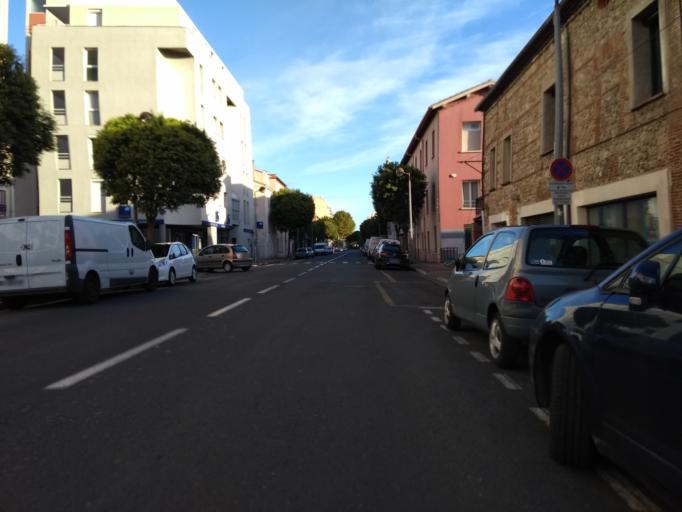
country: FR
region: Languedoc-Roussillon
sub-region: Departement des Pyrenees-Orientales
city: Perpignan
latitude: 42.7125
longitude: 2.8895
